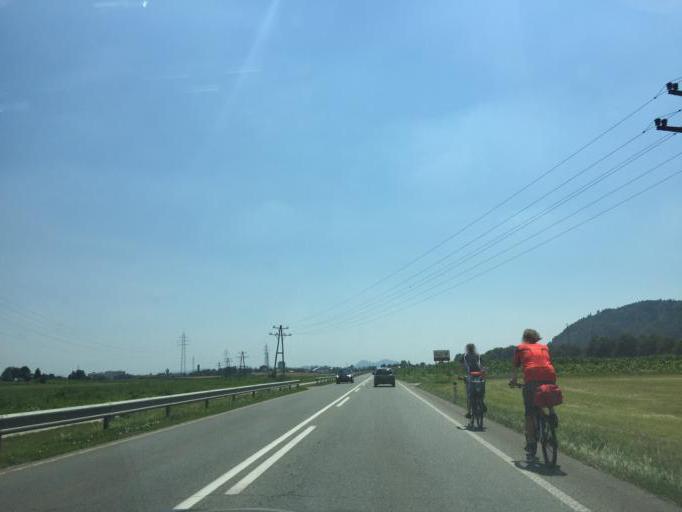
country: SI
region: Naklo
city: Naklo
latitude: 46.2607
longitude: 14.3364
